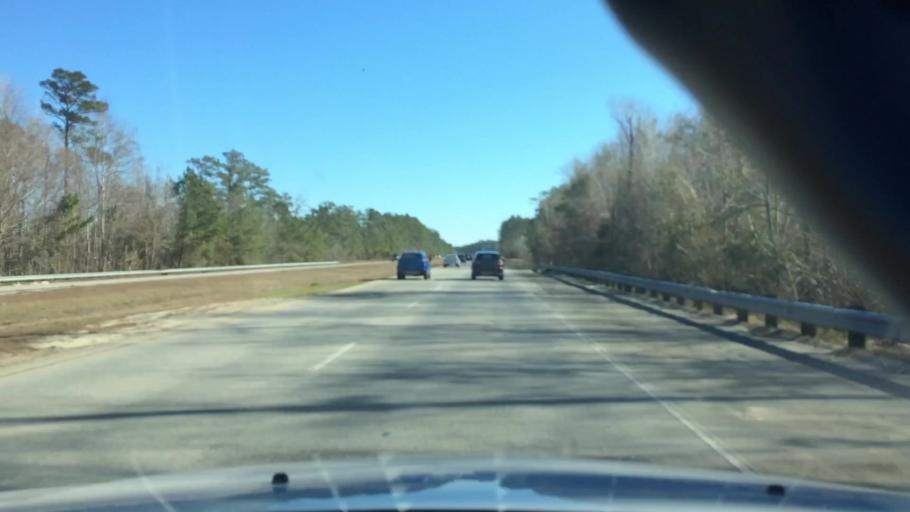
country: US
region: North Carolina
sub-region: Brunswick County
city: Bolivia
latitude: 34.0640
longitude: -78.1938
